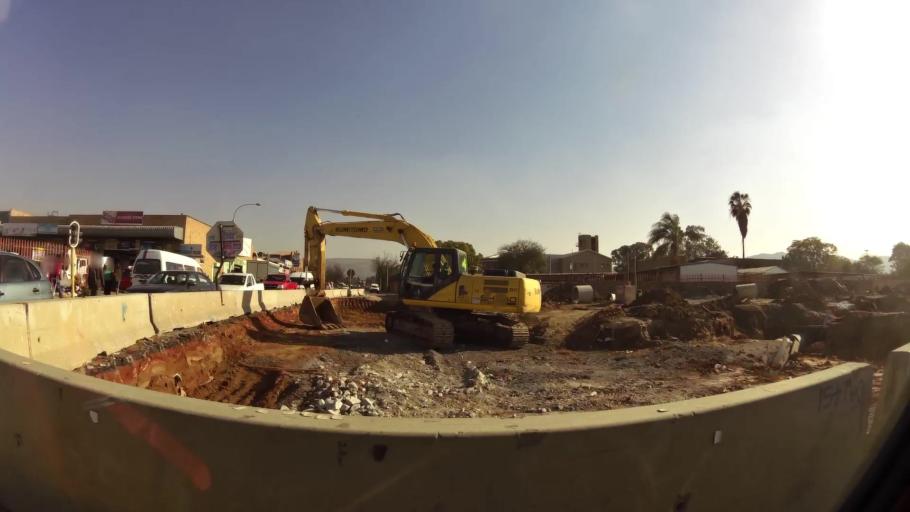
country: ZA
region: North-West
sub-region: Bojanala Platinum District Municipality
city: Rustenburg
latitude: -25.6644
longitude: 27.2352
